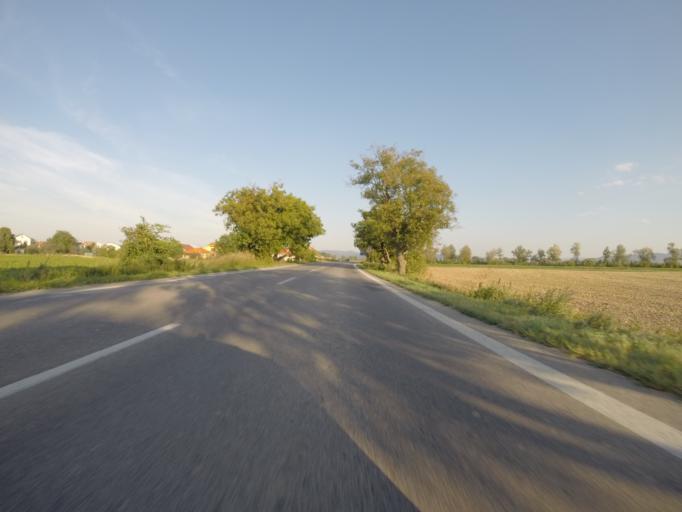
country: SK
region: Nitriansky
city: Banovce nad Bebravou
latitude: 48.6170
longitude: 18.2494
